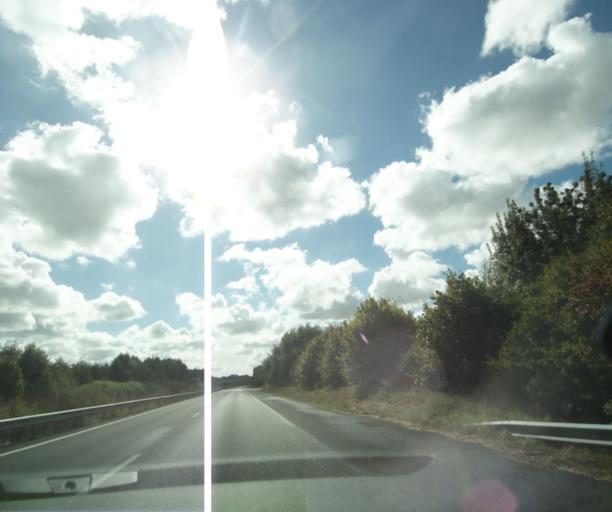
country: FR
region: Poitou-Charentes
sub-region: Departement de la Charente-Maritime
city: Cabariot
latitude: 45.9396
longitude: -0.8451
